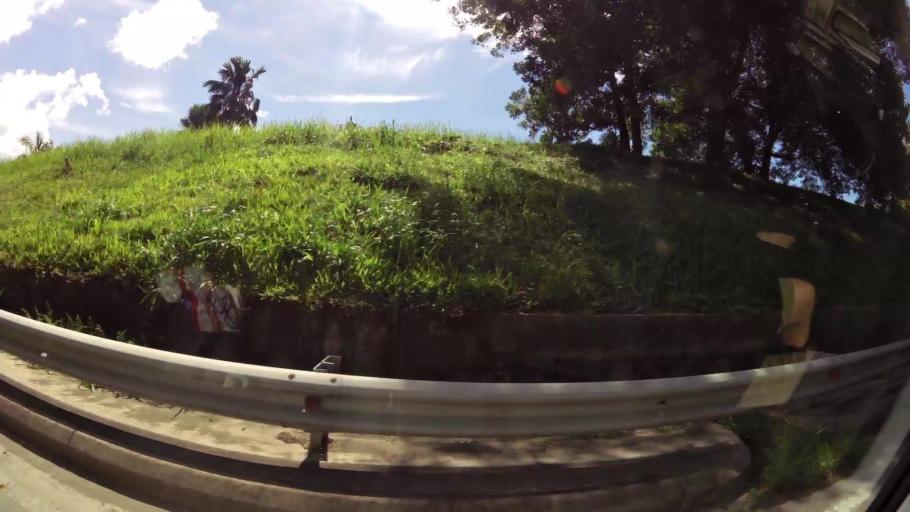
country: BN
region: Brunei and Muara
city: Bandar Seri Begawan
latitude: 4.9710
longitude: 114.9534
